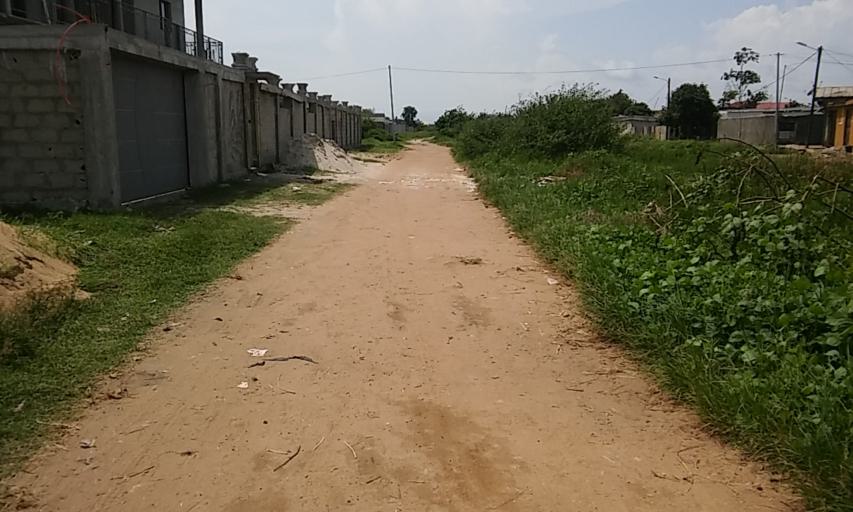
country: CI
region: Sud-Comoe
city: Grand-Bassam
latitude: 5.2182
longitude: -3.7437
